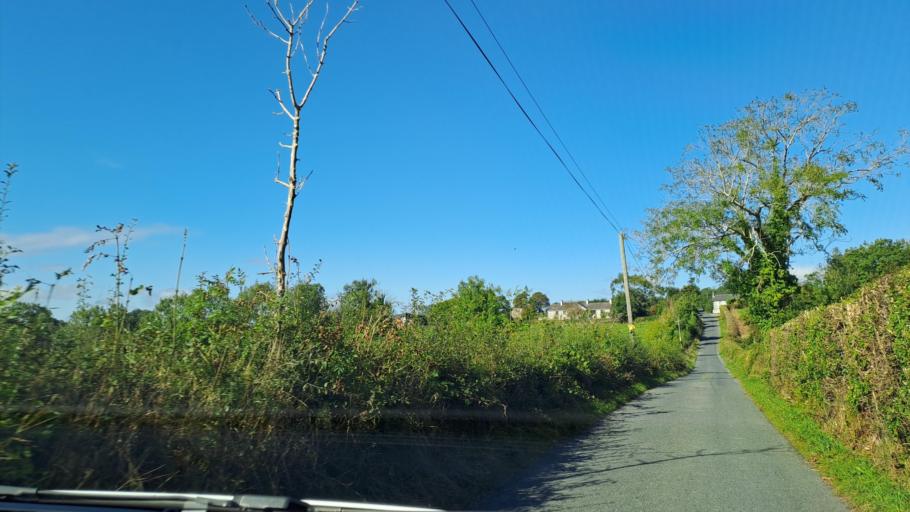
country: IE
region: Ulster
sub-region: County Monaghan
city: Carrickmacross
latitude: 53.9984
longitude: -6.7704
